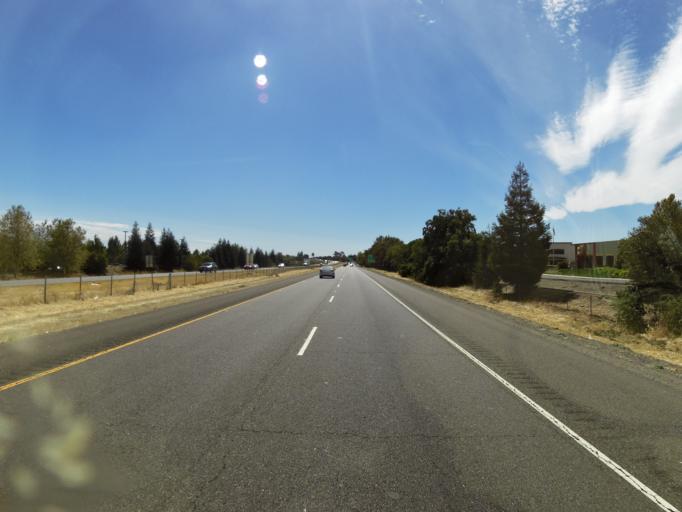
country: US
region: California
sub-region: Solano County
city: Hartley
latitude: 38.3851
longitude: -121.9520
